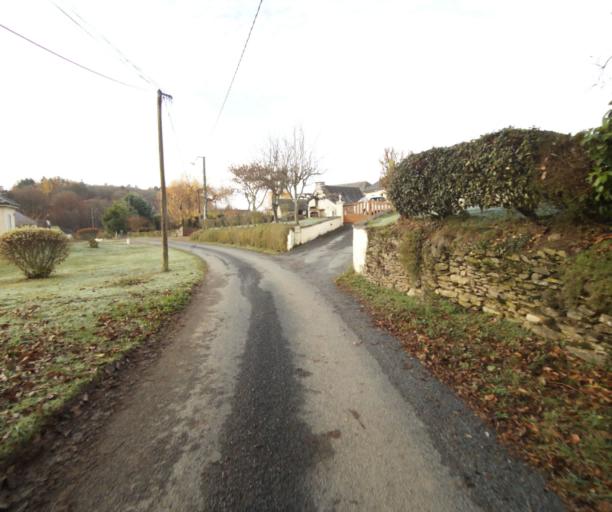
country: FR
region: Limousin
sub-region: Departement de la Correze
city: Cornil
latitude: 45.2134
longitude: 1.7117
